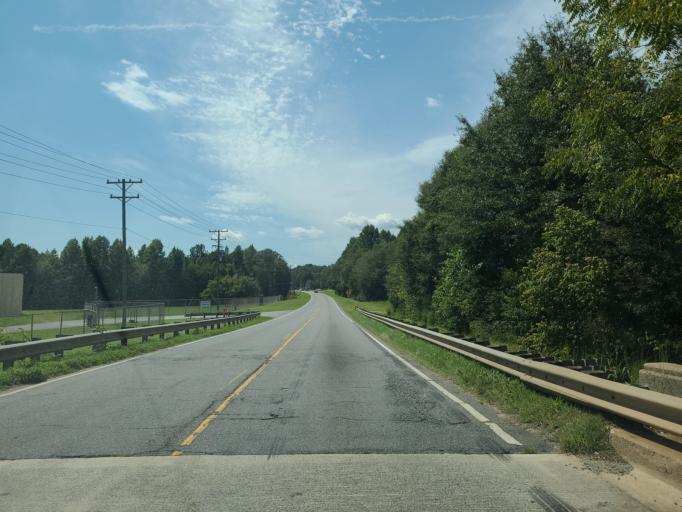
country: US
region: North Carolina
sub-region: Lincoln County
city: Lincolnton
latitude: 35.4459
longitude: -81.2640
